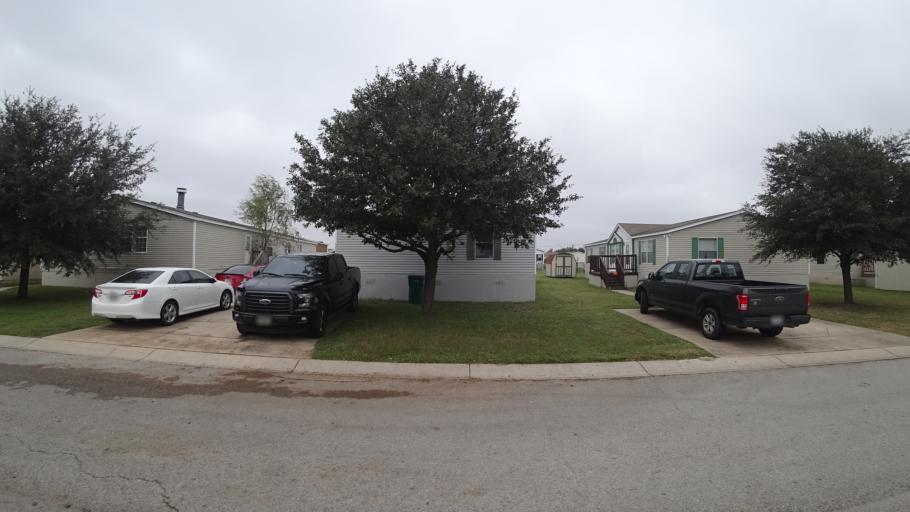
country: US
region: Texas
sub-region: Travis County
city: Pflugerville
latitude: 30.4113
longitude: -97.6072
